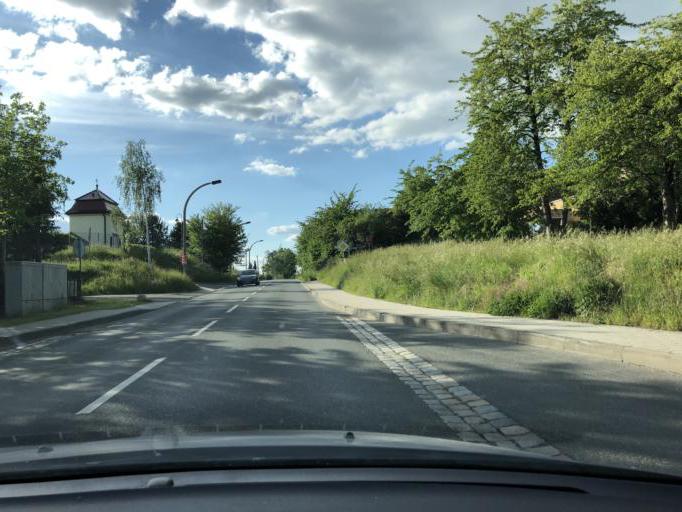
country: DE
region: Thuringia
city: Schmolln
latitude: 50.8927
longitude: 12.3648
